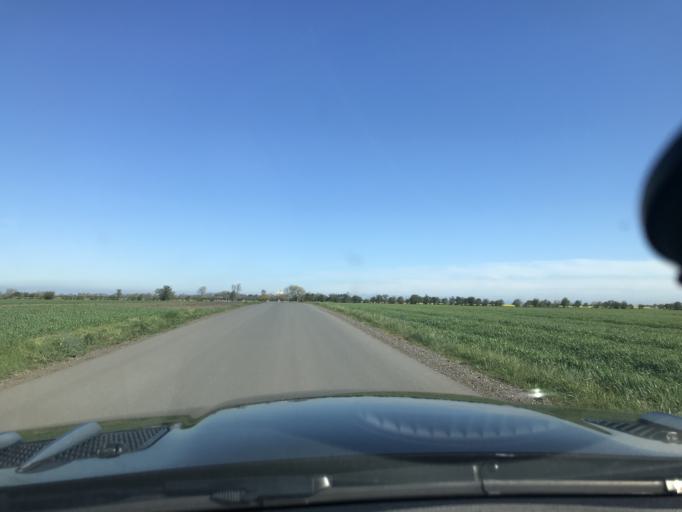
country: DE
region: Schleswig-Holstein
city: Grossenbrode
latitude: 54.4365
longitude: 11.1169
